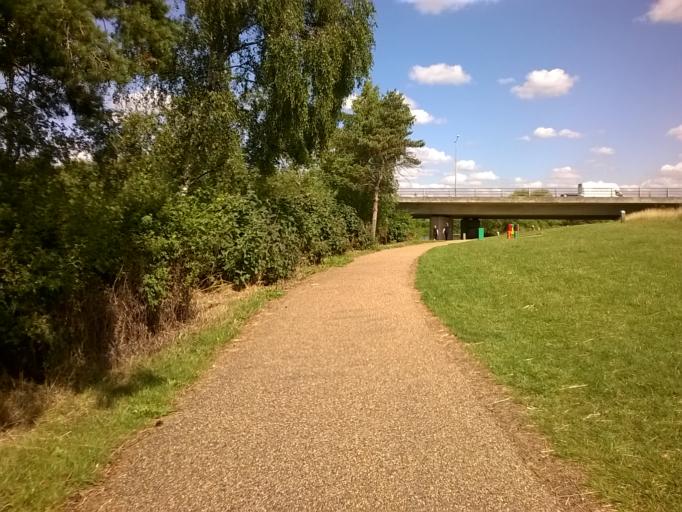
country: GB
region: England
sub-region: Milton Keynes
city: Broughton
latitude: 52.0539
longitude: -0.7156
